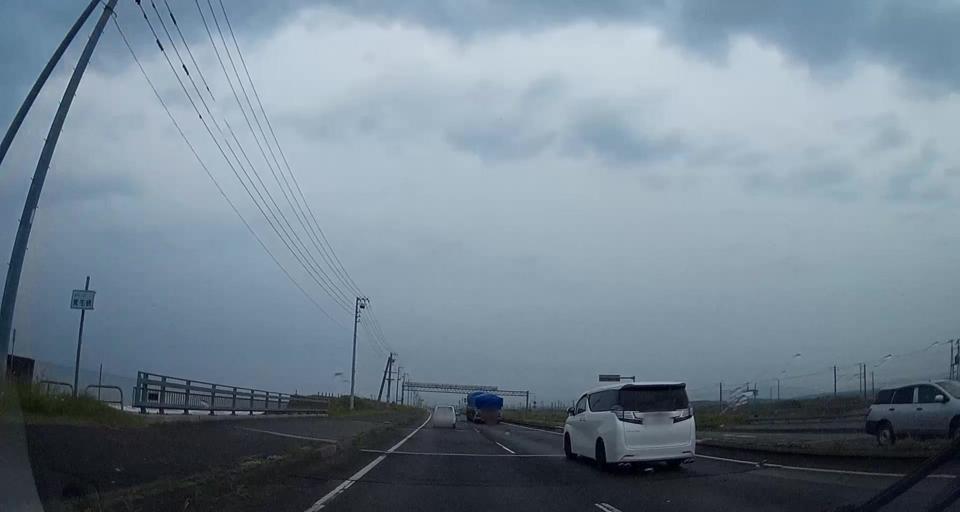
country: JP
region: Hokkaido
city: Shiraoi
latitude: 42.5932
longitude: 141.4618
